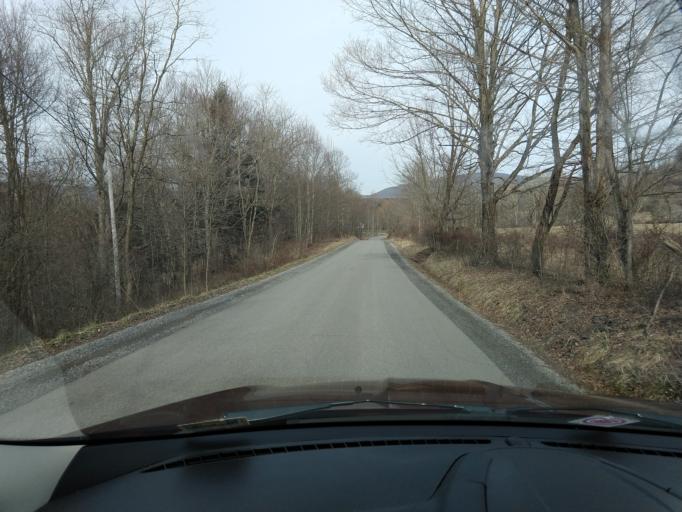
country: US
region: West Virginia
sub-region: Tucker County
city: Parsons
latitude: 39.0046
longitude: -79.5020
